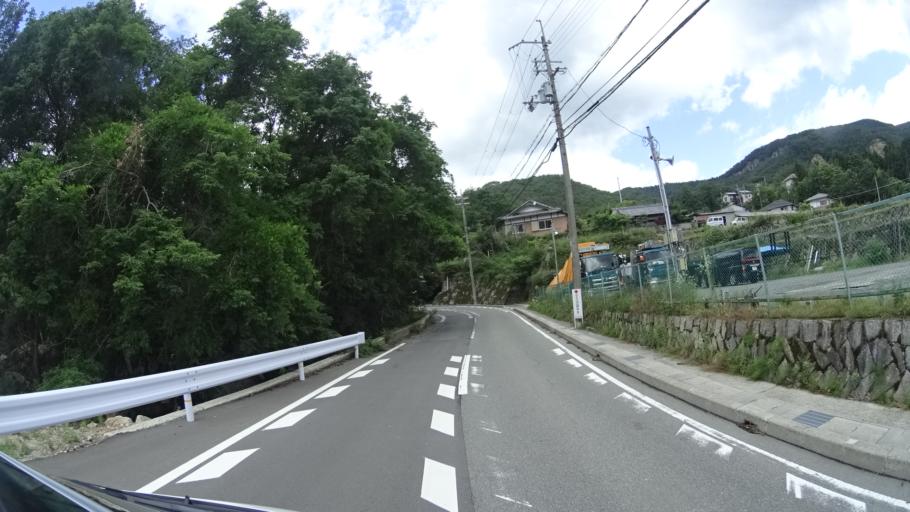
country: JP
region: Kyoto
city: Kameoka
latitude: 35.0153
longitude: 135.4275
